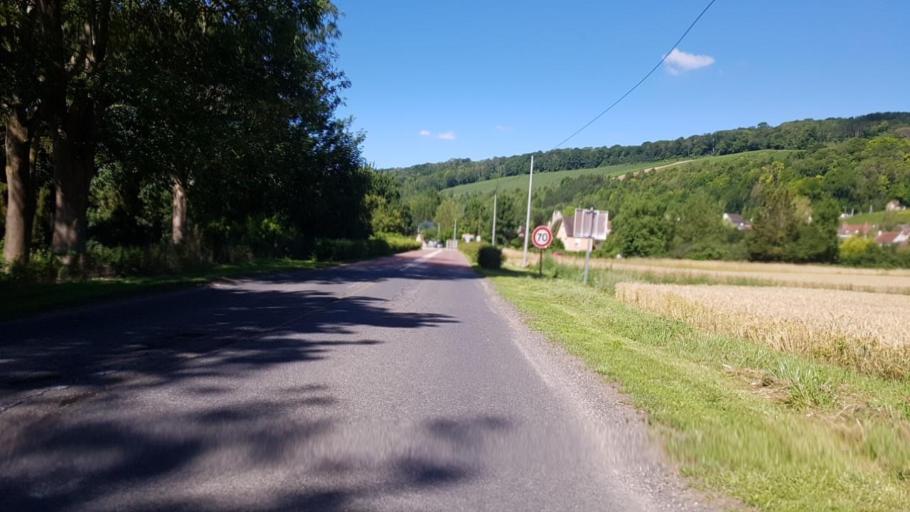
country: FR
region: Ile-de-France
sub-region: Departement de Seine-et-Marne
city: Saacy-sur-Marne
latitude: 48.9779
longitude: 3.2260
